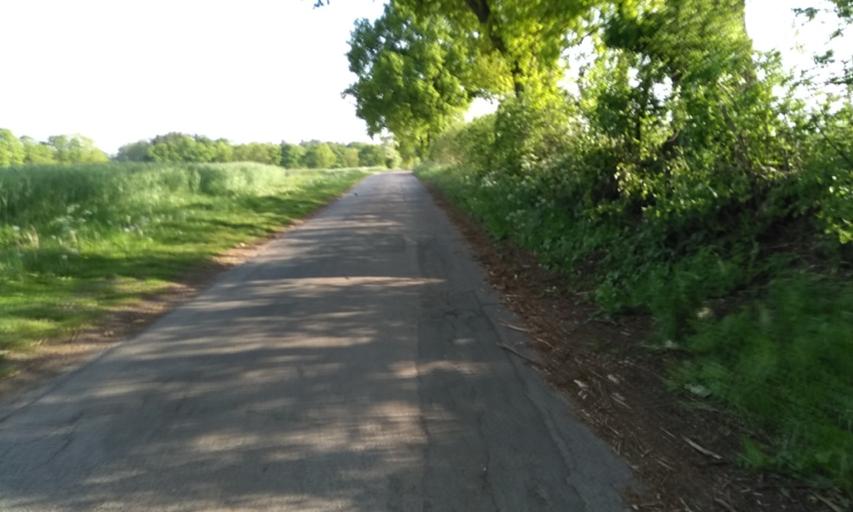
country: DE
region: Lower Saxony
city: Horneburg
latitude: 53.5024
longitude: 9.5643
